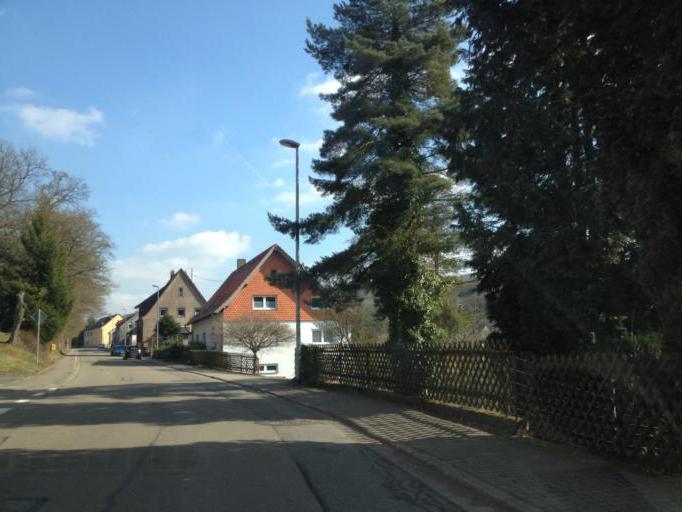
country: DE
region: Rheinland-Pfalz
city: Breitenbach
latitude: 49.4619
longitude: 7.2414
